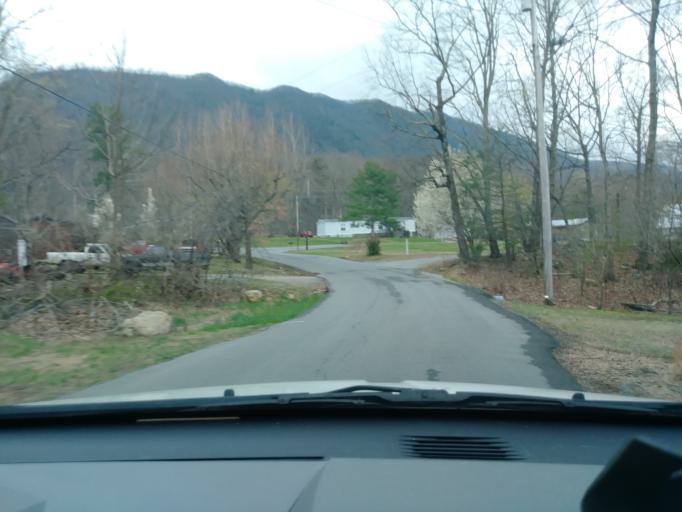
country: US
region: Tennessee
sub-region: Greene County
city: Tusculum
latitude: 36.0740
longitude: -82.7230
